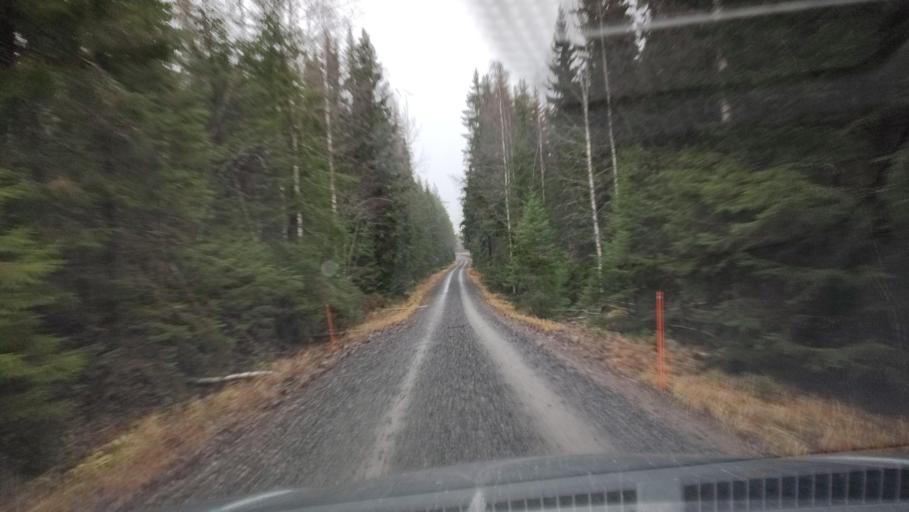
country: FI
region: Southern Ostrobothnia
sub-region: Suupohja
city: Karijoki
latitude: 62.1408
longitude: 21.6274
